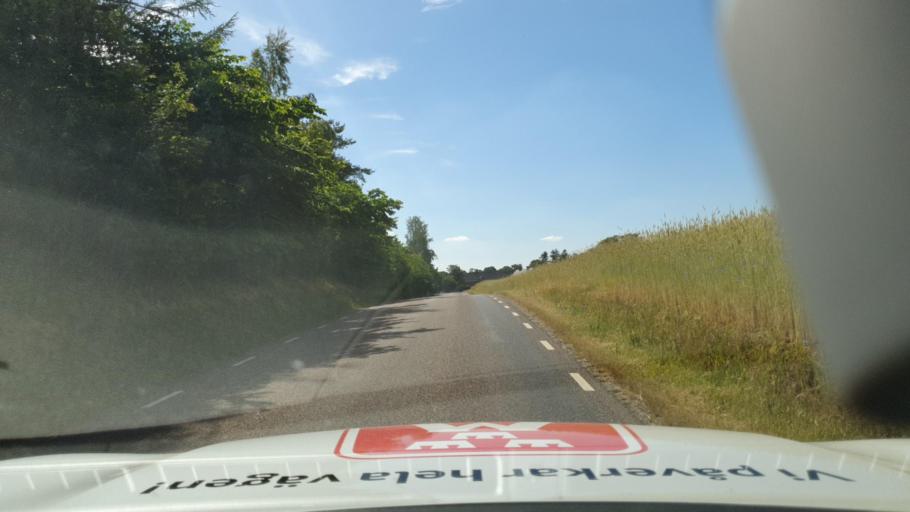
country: SE
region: Skane
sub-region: Sjobo Kommun
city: Blentarp
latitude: 55.6052
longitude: 13.5982
